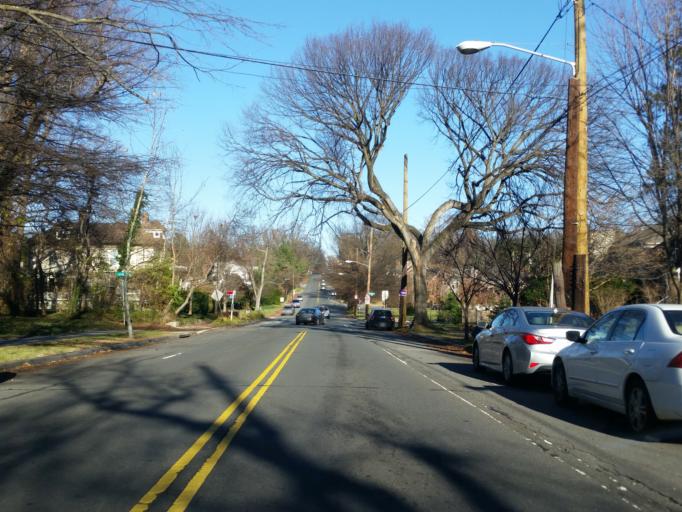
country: US
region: Maryland
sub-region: Montgomery County
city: Friendship Village
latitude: 38.9528
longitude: -77.0959
